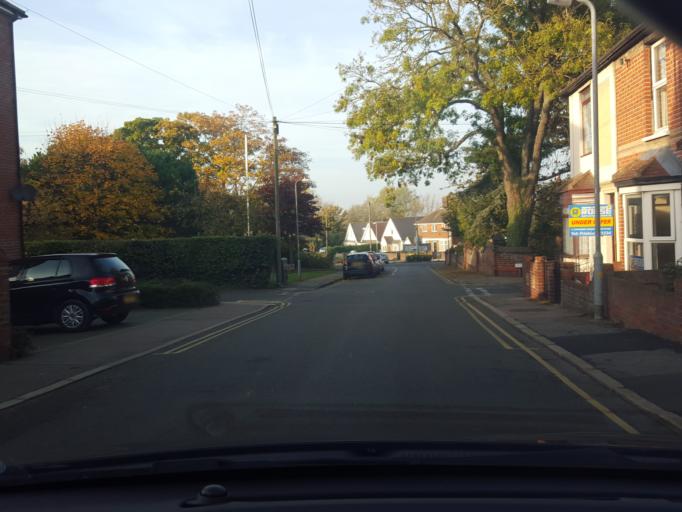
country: GB
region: England
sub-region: Essex
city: Walton-on-the-Naze
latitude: 51.8476
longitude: 1.2680
